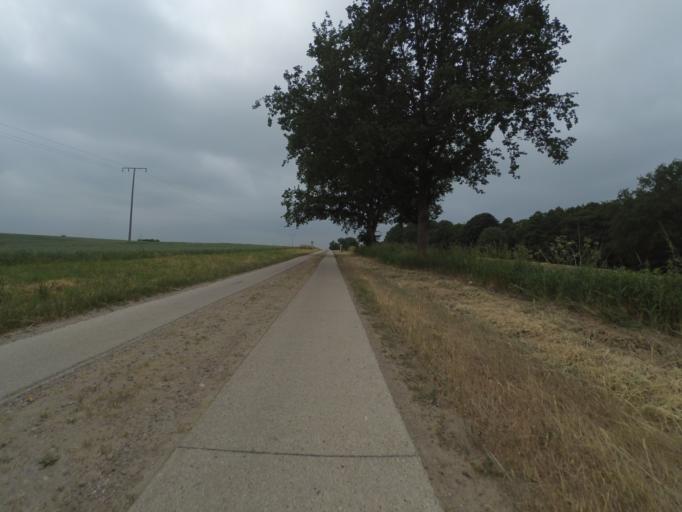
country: DE
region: Mecklenburg-Vorpommern
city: Goldberg
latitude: 53.5177
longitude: 12.0935
